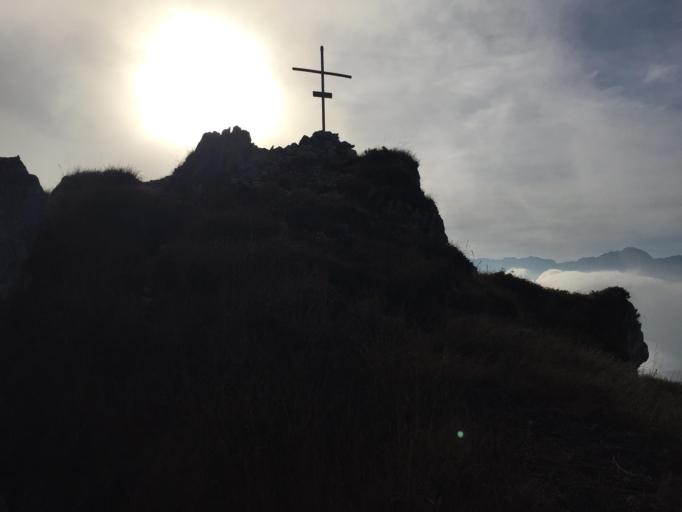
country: IT
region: Friuli Venezia Giulia
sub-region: Provincia di Udine
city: Moggio Udinese
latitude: 46.4527
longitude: 13.2098
